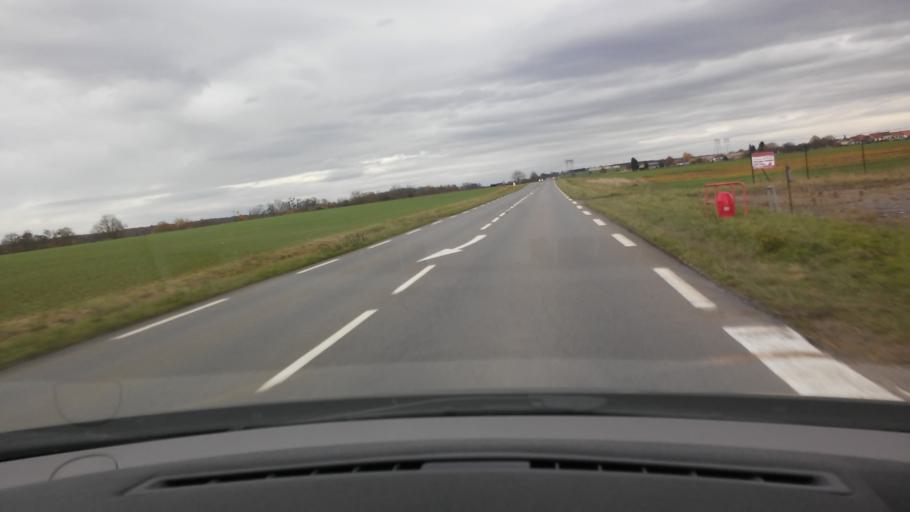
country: FR
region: Lorraine
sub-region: Departement de la Moselle
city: Retonfey
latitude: 49.1528
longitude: 6.2609
